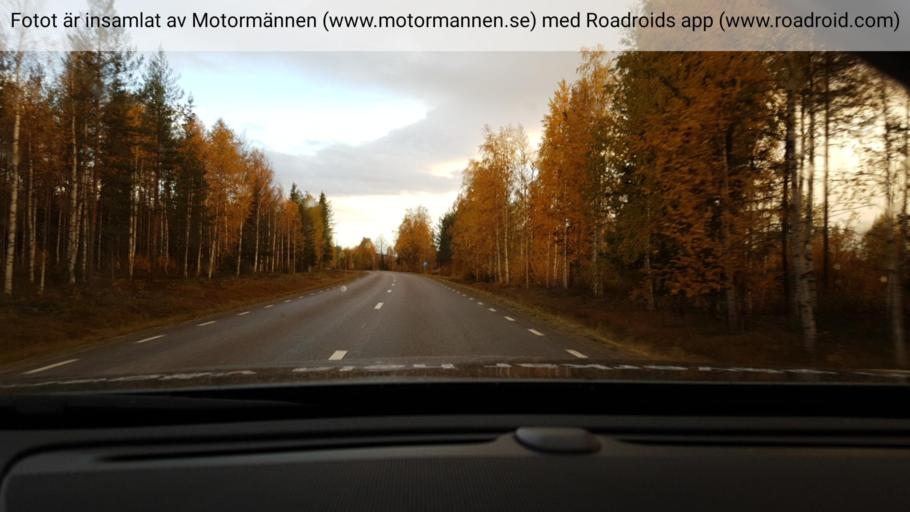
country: SE
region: Norrbotten
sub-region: Overkalix Kommun
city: OEverkalix
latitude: 66.5054
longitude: 22.7647
